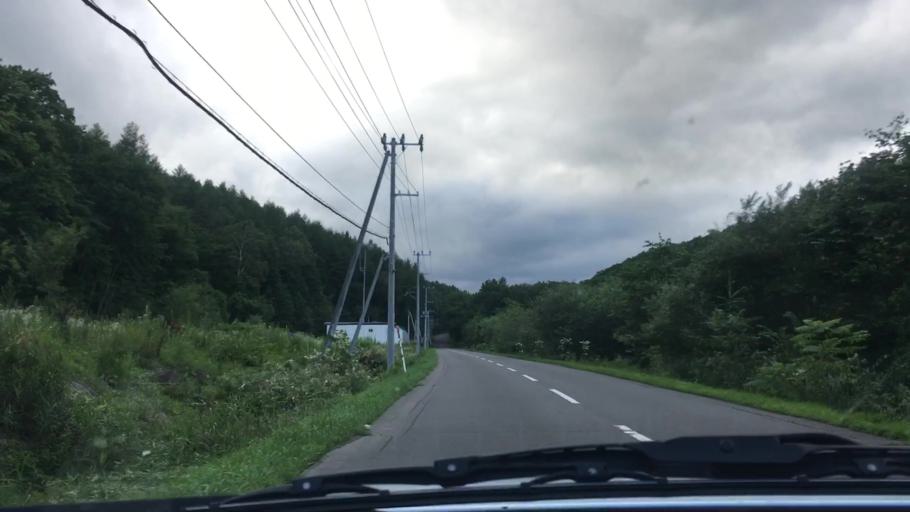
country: JP
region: Hokkaido
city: Otofuke
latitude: 43.1428
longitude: 142.8817
